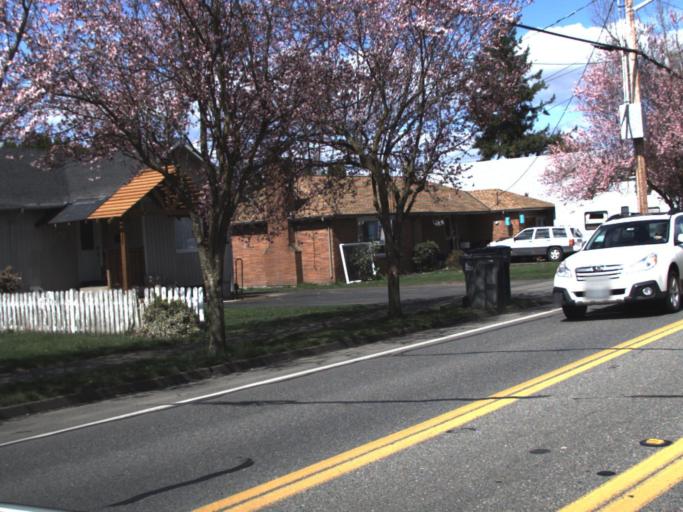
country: US
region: Washington
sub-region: King County
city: Enumclaw
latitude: 47.2133
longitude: -121.9896
